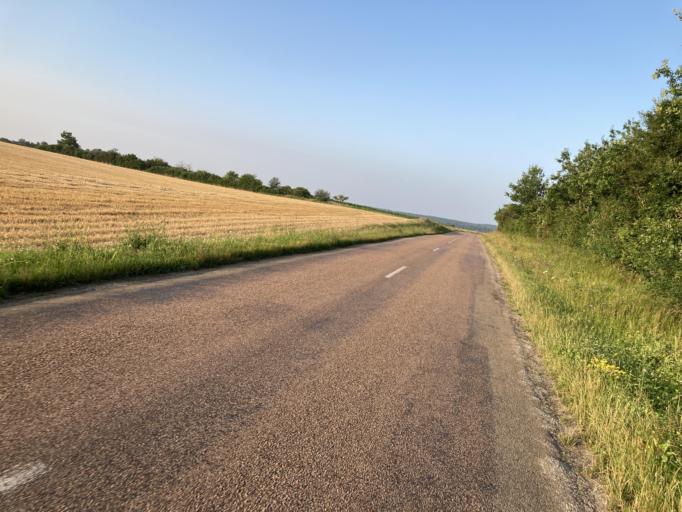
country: FR
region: Bourgogne
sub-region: Departement de l'Yonne
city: Vermenton
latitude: 47.6006
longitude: 3.6568
